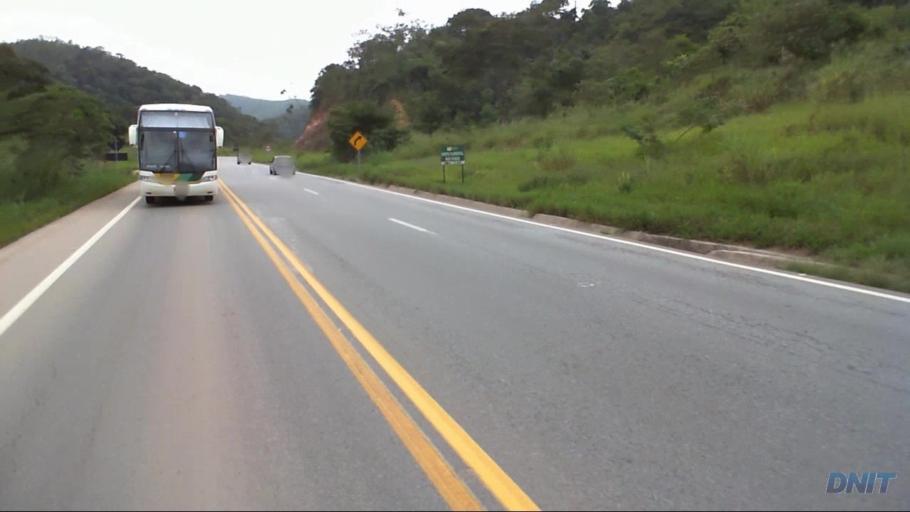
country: BR
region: Minas Gerais
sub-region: Nova Era
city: Nova Era
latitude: -19.6410
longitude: -42.9171
